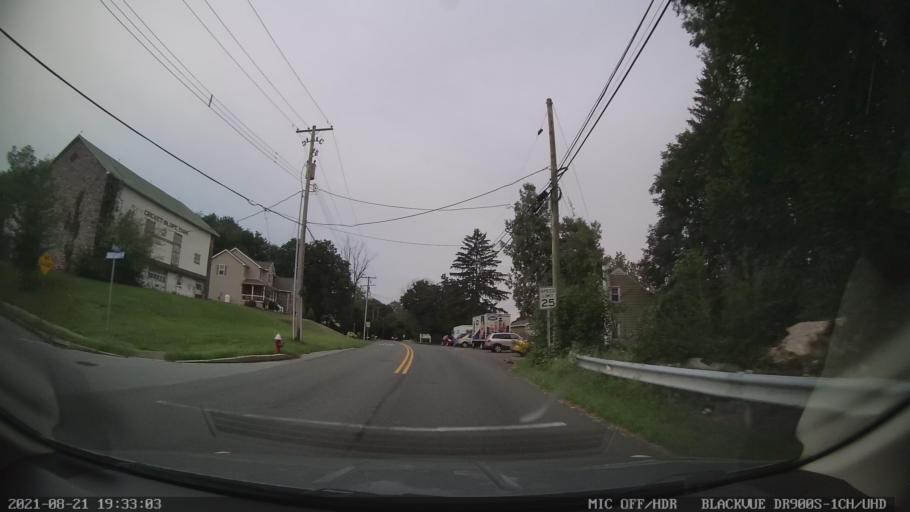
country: US
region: Pennsylvania
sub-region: Berks County
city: Oley
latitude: 40.3947
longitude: -75.7976
